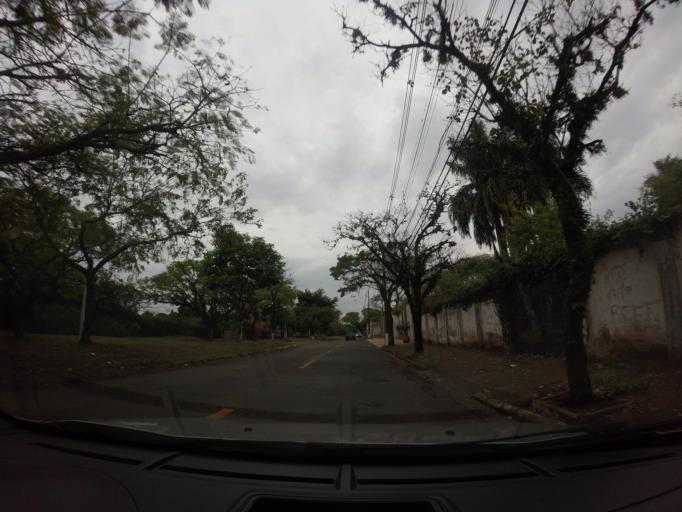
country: BR
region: Sao Paulo
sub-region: Piracicaba
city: Piracicaba
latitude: -22.7574
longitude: -47.5941
